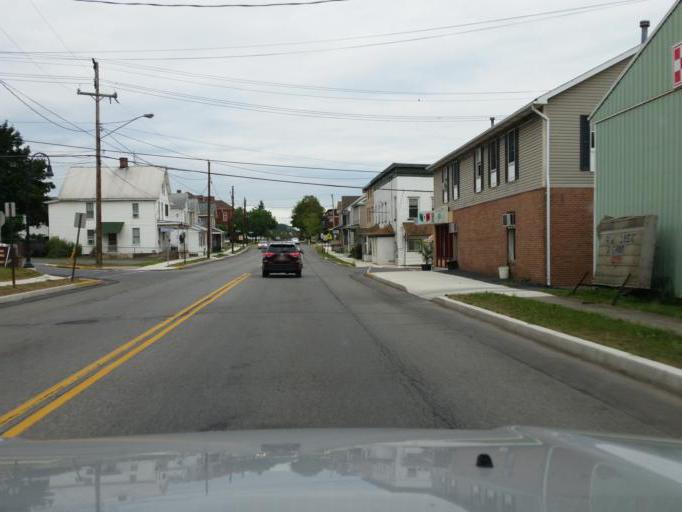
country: US
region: Pennsylvania
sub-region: Blair County
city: Hollidaysburg
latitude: 40.4273
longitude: -78.3938
